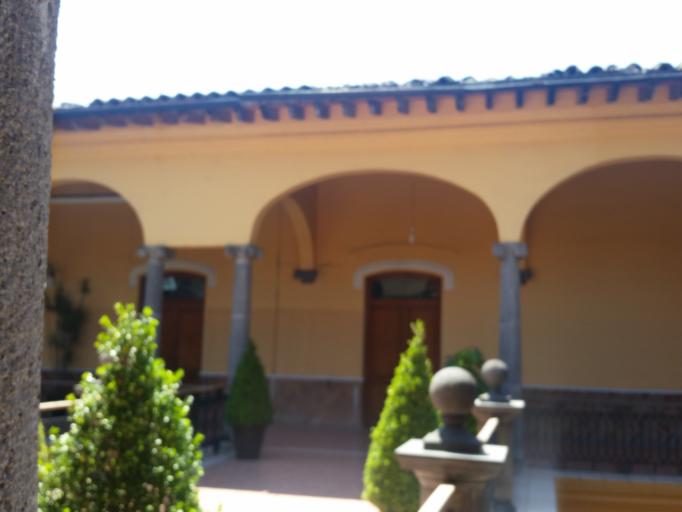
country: MX
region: Veracruz
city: Coatepec
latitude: 19.4546
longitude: -96.9604
